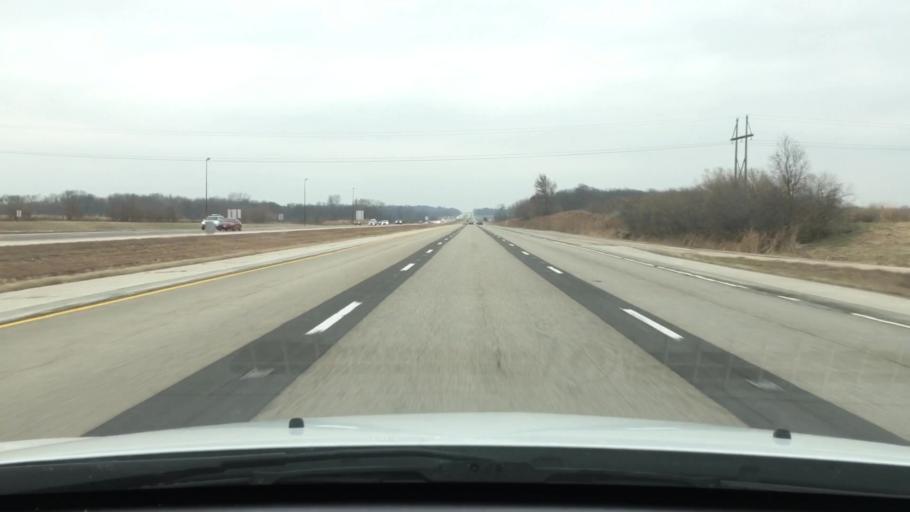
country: US
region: Illinois
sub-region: Logan County
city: Lincoln
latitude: 40.1156
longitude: -89.4164
